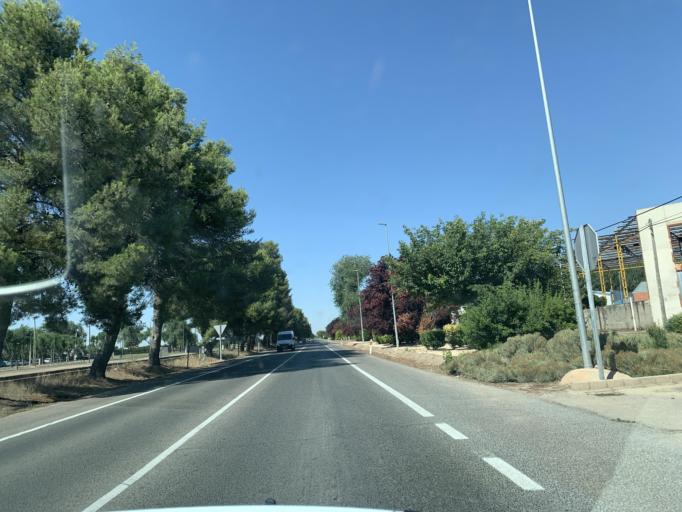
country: ES
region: Castille-La Mancha
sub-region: Provincia de Ciudad Real
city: Argamasilla de Alba
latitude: 39.1308
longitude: -3.0811
